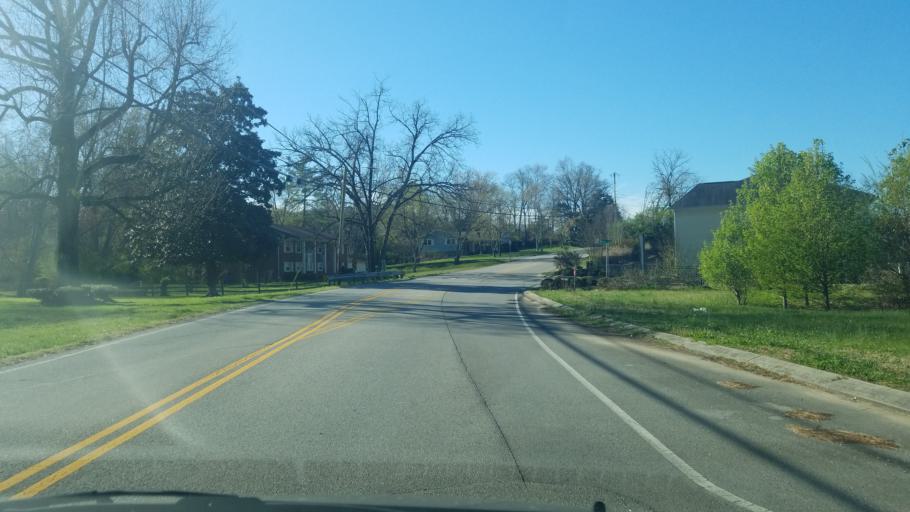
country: US
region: Tennessee
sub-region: Hamilton County
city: East Brainerd
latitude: 35.0209
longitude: -85.1729
